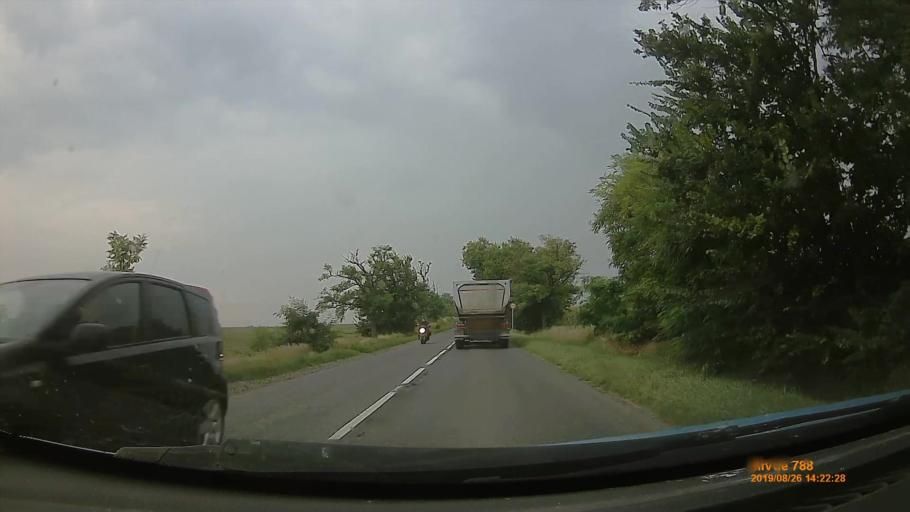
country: HU
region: Fejer
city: Csakvar
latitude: 47.3715
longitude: 18.4437
